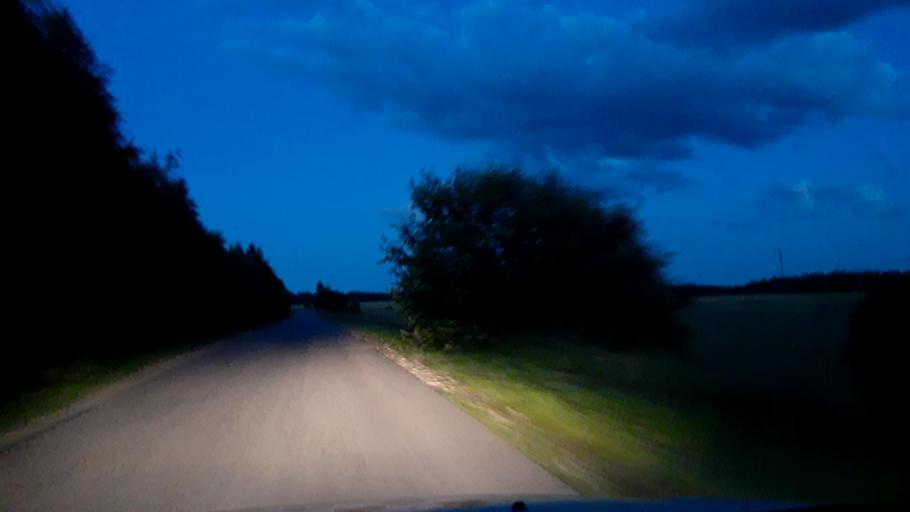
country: RU
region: Nizjnij Novgorod
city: Pamyat' Parizhskoy Kommuny
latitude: 56.0612
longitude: 44.4685
